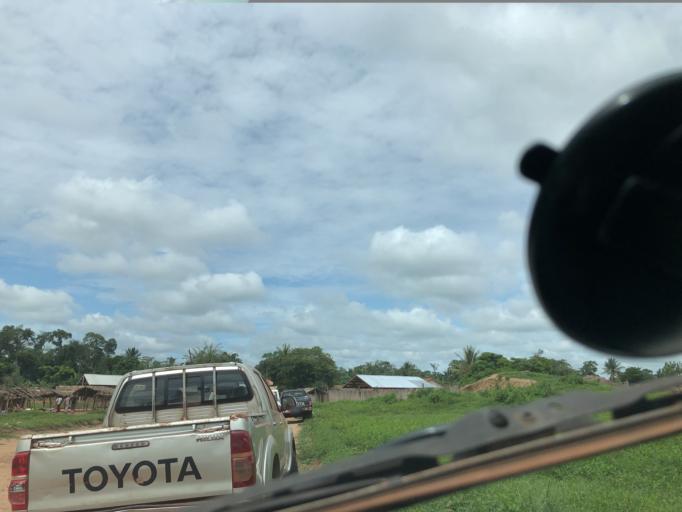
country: CD
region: Equateur
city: Gemena
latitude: 3.3201
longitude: 19.3916
